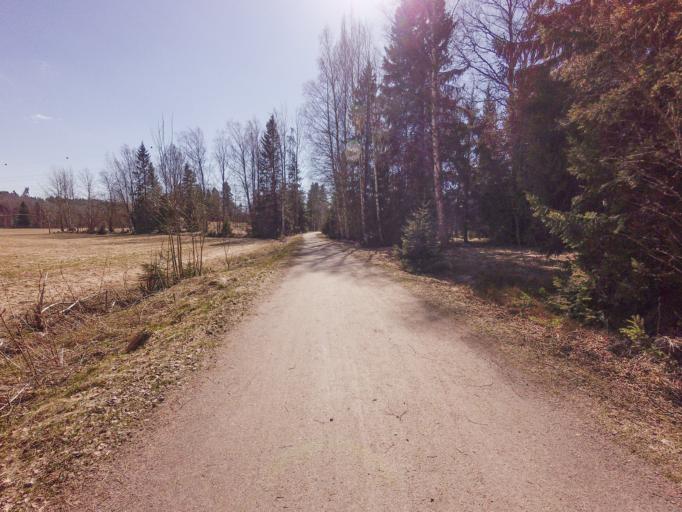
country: FI
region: Uusimaa
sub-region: Helsinki
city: Vantaa
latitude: 60.2146
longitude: 25.0246
